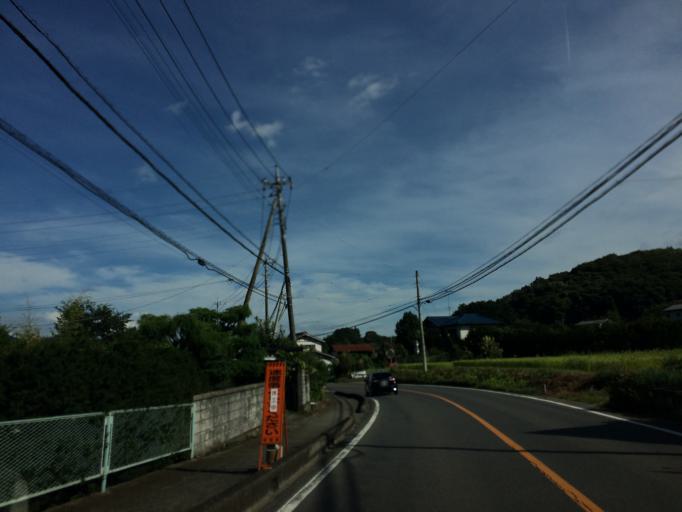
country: JP
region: Gunma
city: Nakanojomachi
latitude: 36.5684
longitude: 138.8727
